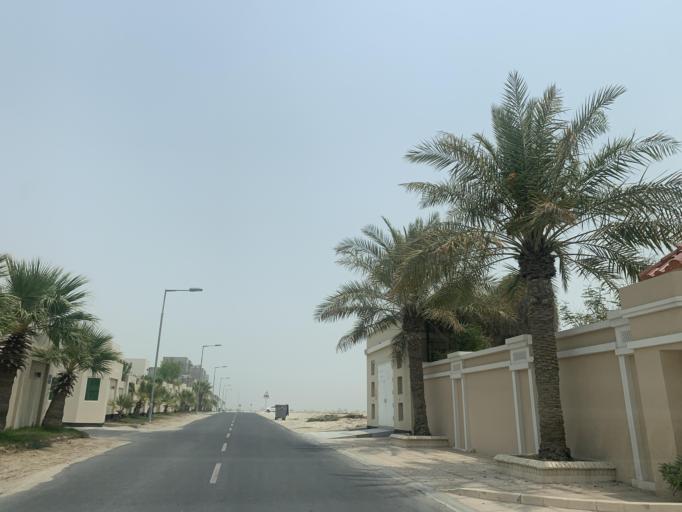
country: BH
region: Central Governorate
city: Madinat Hamad
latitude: 26.1691
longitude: 50.4792
